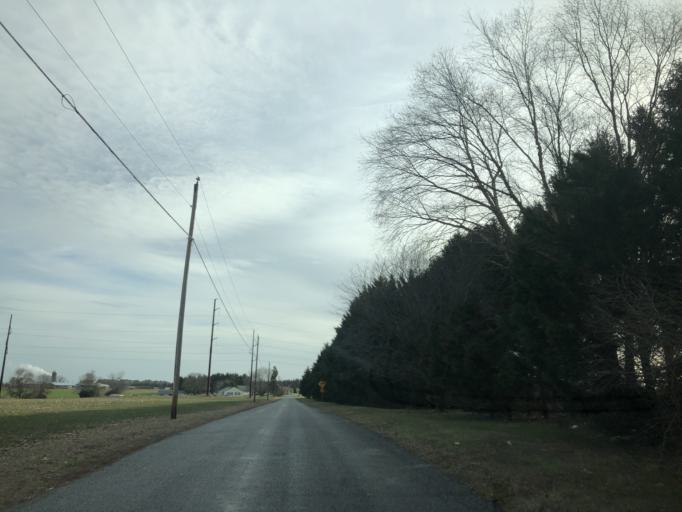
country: US
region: Delaware
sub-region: New Castle County
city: Middletown
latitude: 39.4531
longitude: -75.6373
